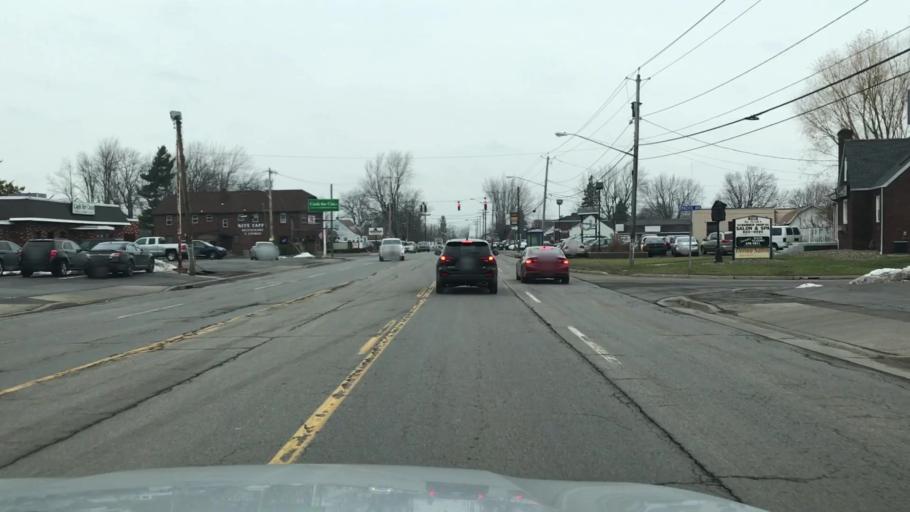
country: US
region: New York
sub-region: Erie County
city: Lackawanna
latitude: 42.8158
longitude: -78.8007
